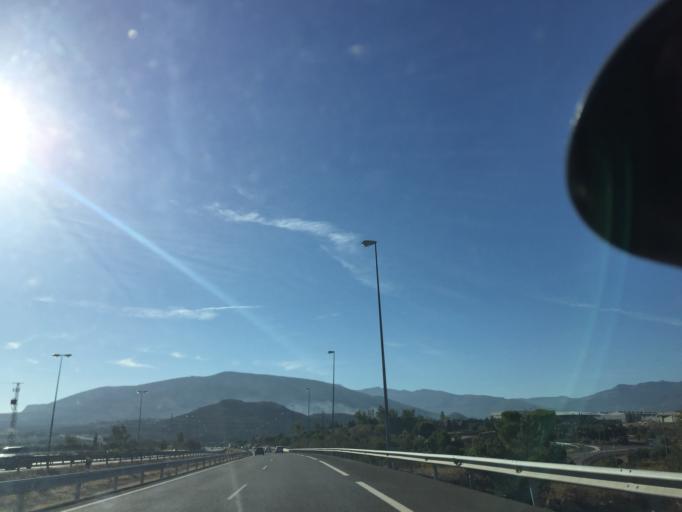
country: ES
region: Andalusia
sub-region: Provincia de Jaen
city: Jaen
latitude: 37.7856
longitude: -3.7562
